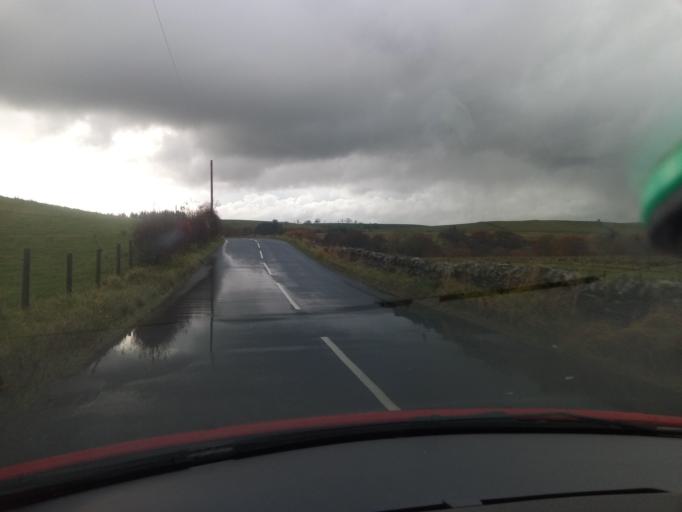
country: GB
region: England
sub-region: Northumberland
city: Birtley
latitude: 55.1115
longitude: -2.2408
